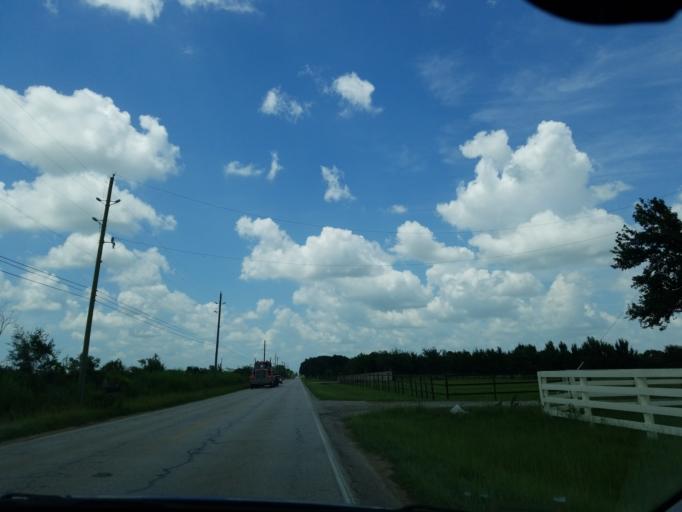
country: US
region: Texas
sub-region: Harris County
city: Katy
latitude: 29.8555
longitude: -95.8074
